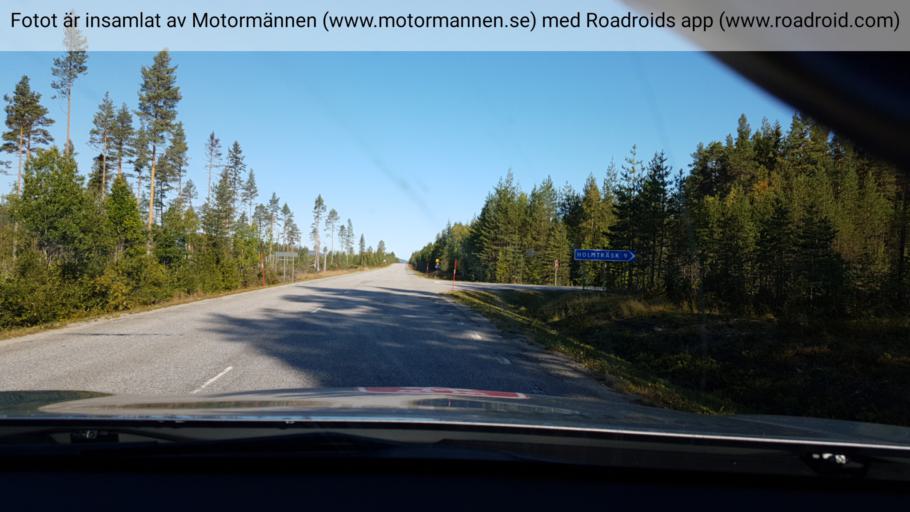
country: SE
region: Vaesterbotten
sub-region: Norsjo Kommun
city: Norsjoe
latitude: 64.5466
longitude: 19.3351
